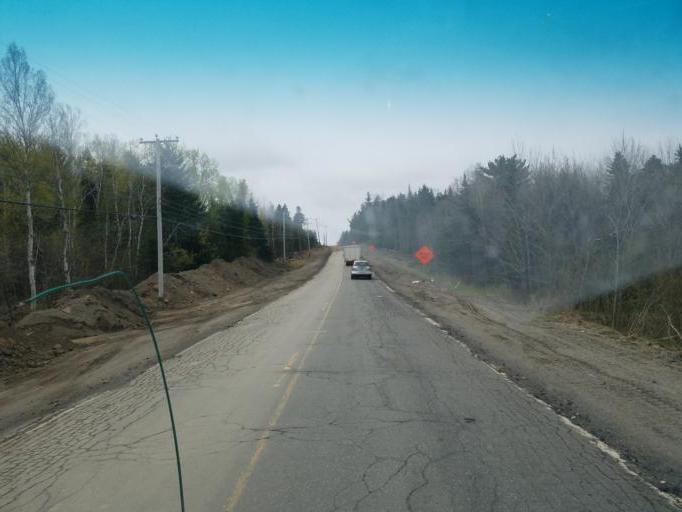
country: US
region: Maine
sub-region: Washington County
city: East Machias
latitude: 44.7762
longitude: -67.1961
